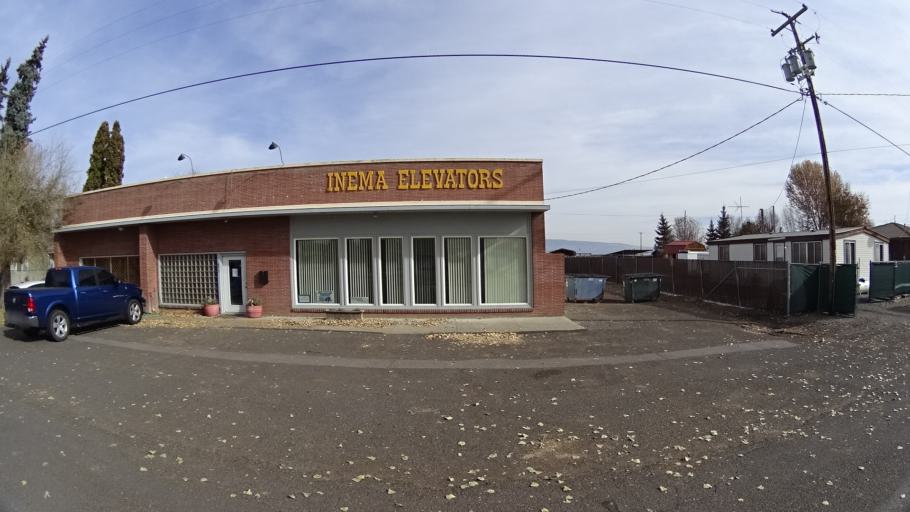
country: US
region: California
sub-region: Siskiyou County
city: Tulelake
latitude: 41.9546
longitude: -121.4730
